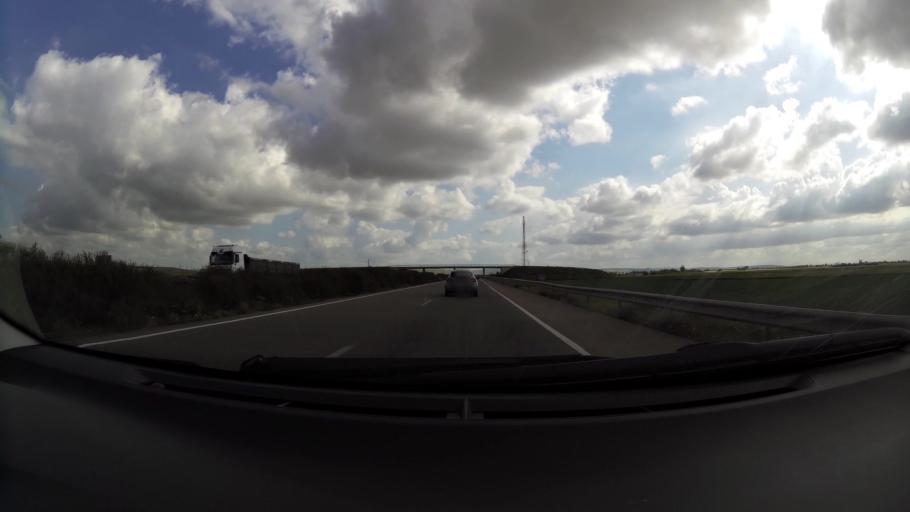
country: MA
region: Chaouia-Ouardigha
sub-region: Settat Province
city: Berrechid
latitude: 33.1378
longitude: -7.5764
